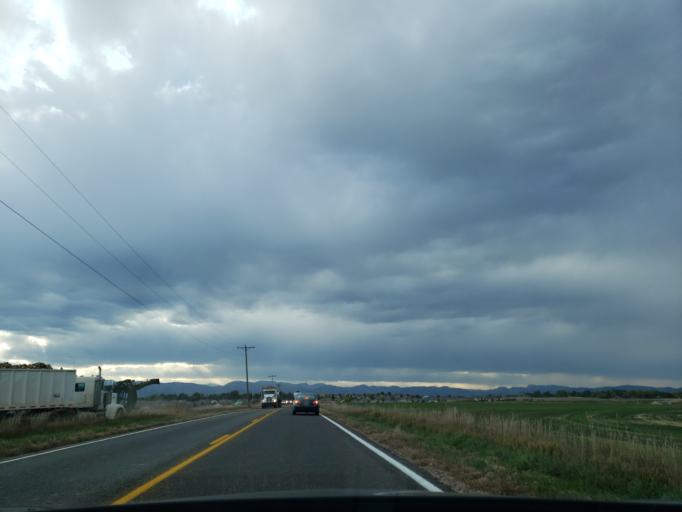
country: US
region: Colorado
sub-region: Larimer County
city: Fort Collins
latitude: 40.6247
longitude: -105.0242
